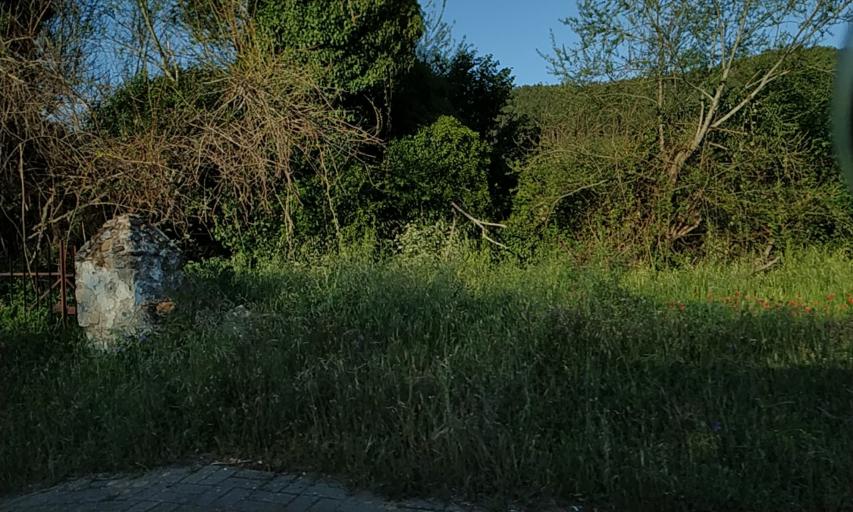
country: PT
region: Portalegre
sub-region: Marvao
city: Marvao
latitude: 39.3782
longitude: -7.3884
